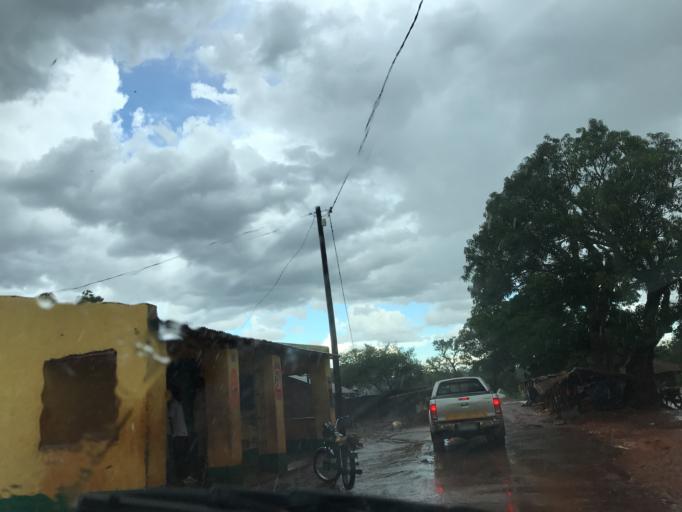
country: MZ
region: Nampula
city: Nacala
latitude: -14.7477
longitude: 39.9800
